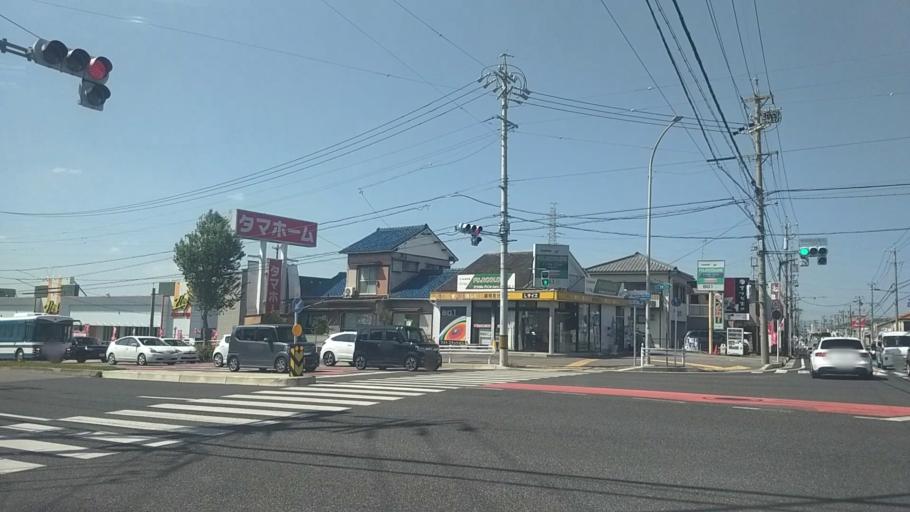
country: JP
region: Aichi
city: Okazaki
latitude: 34.9790
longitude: 137.1696
